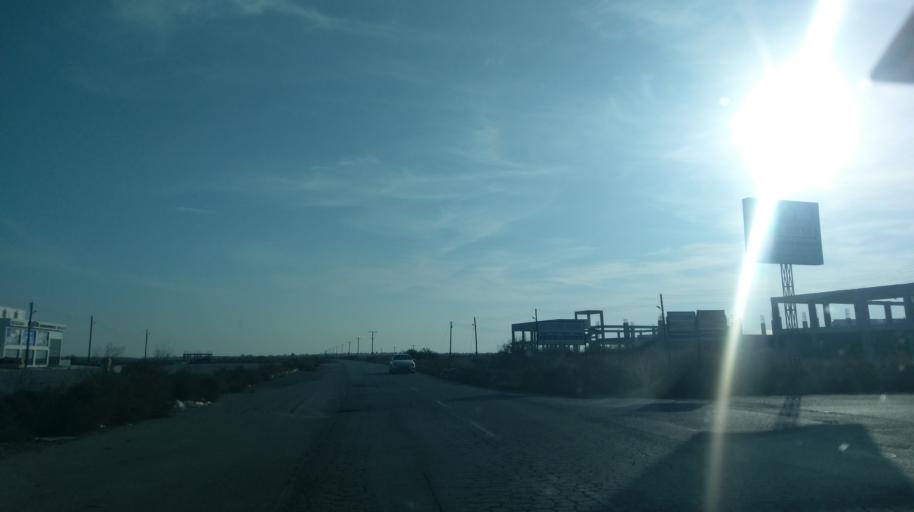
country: CY
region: Ammochostos
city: Acheritou
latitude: 35.1336
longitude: 33.8718
